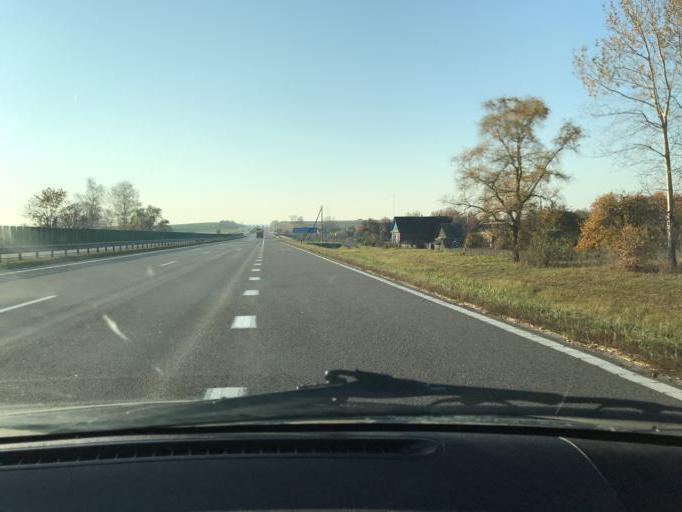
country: BY
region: Minsk
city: Loshnitsa
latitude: 54.2899
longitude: 28.8119
